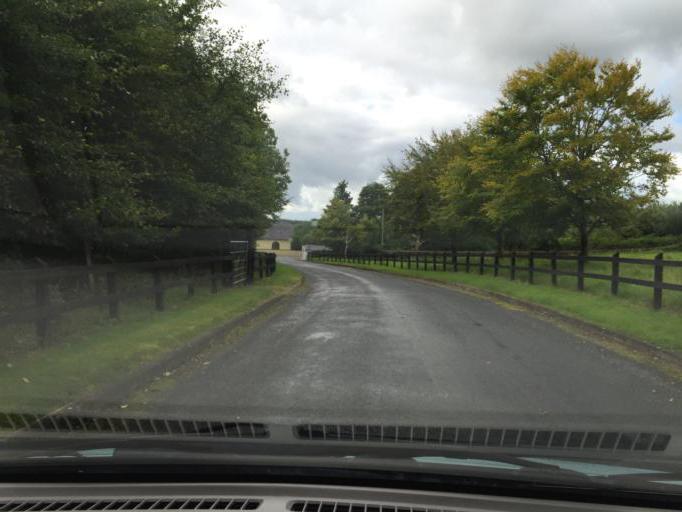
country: IE
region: Connaught
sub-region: Sligo
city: Tobercurry
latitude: 54.0380
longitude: -8.8183
